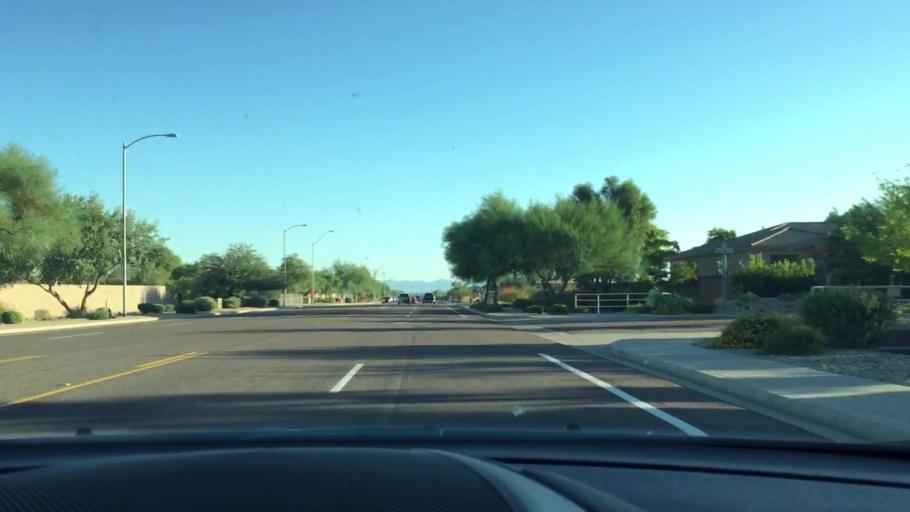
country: US
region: Arizona
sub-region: Maricopa County
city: Sun City West
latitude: 33.7046
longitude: -112.2377
